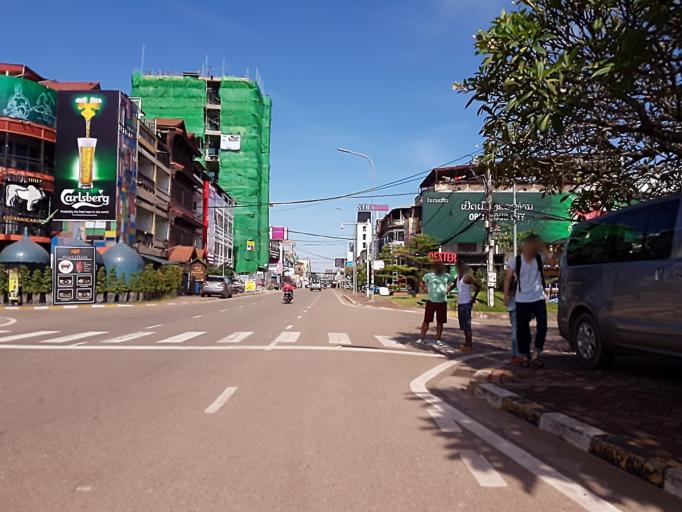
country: LA
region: Vientiane
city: Vientiane
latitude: 17.9670
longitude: 102.6070
